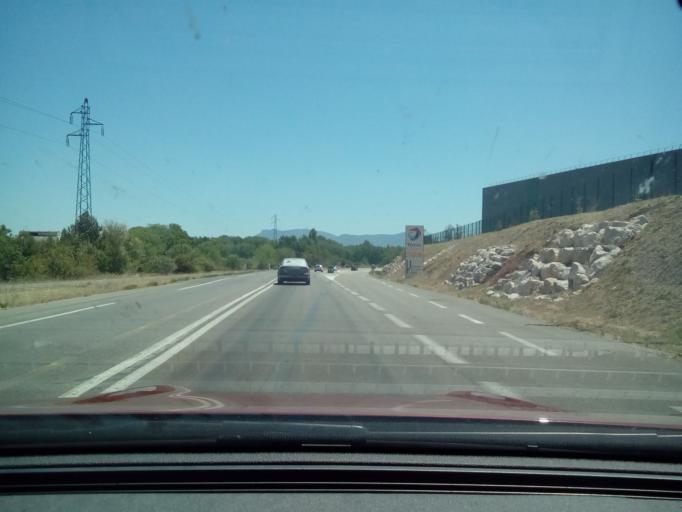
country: FR
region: Provence-Alpes-Cote d'Azur
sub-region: Departement des Bouches-du-Rhone
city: Rousset
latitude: 43.4684
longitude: 5.5996
